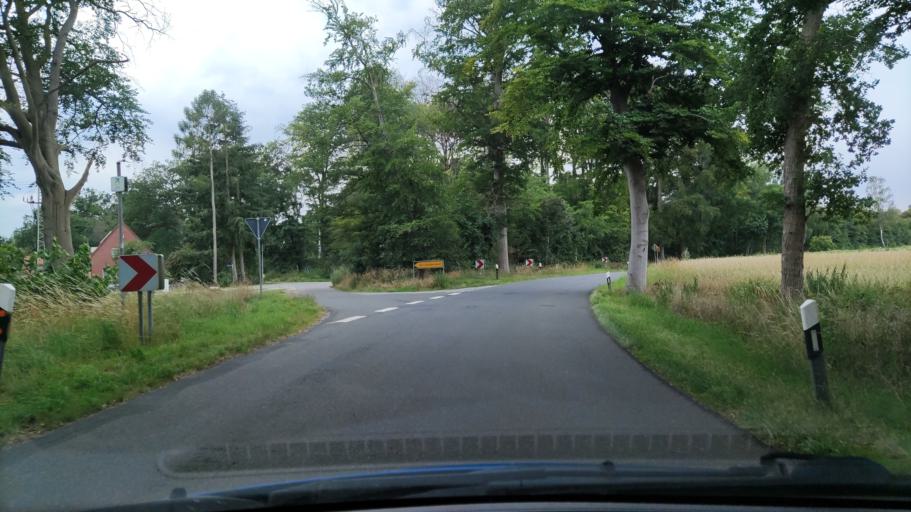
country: DE
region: Lower Saxony
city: Suhlendorf
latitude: 52.9665
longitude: 10.8083
